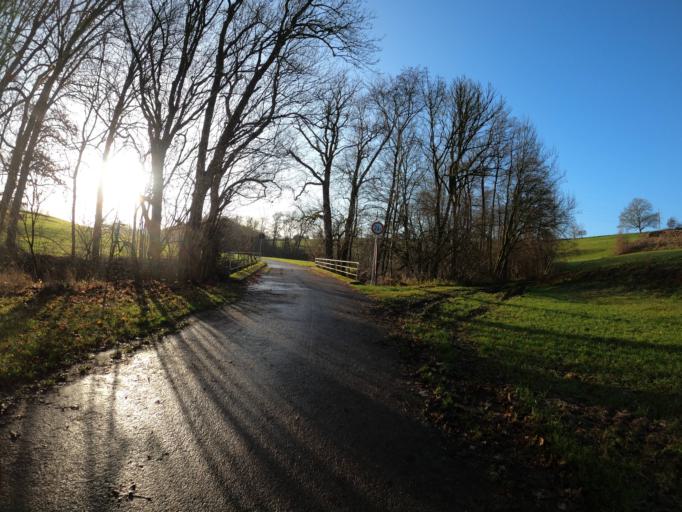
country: DE
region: Baden-Wuerttemberg
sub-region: Regierungsbezirk Stuttgart
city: Wangen
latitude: 48.6982
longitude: 9.6166
